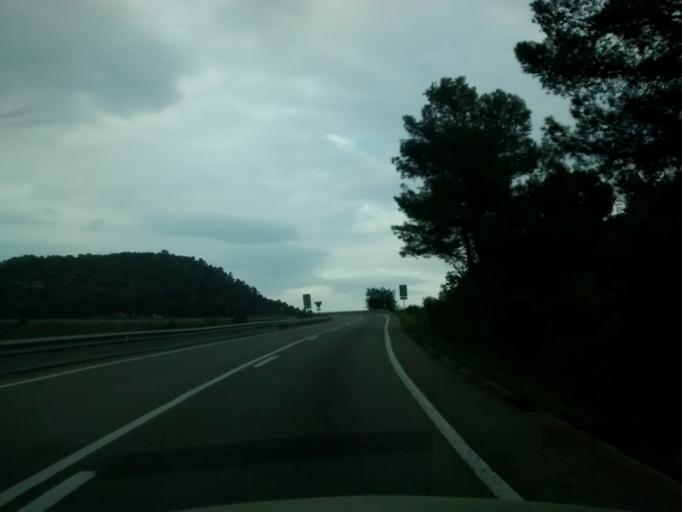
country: ES
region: Catalonia
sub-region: Provincia de Tarragona
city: Benifallet
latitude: 40.9913
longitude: 0.5151
